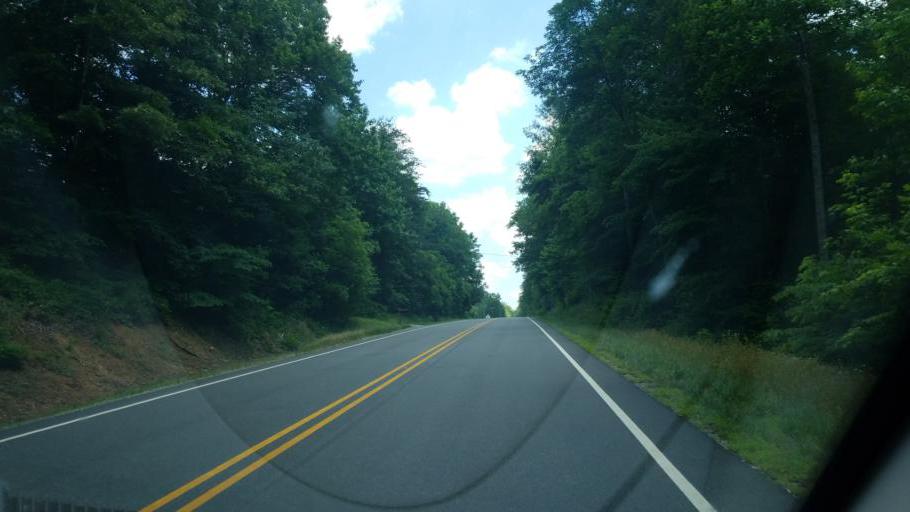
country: US
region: Virginia
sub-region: Cumberland County
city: Cumberland
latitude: 37.4826
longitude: -78.3152
